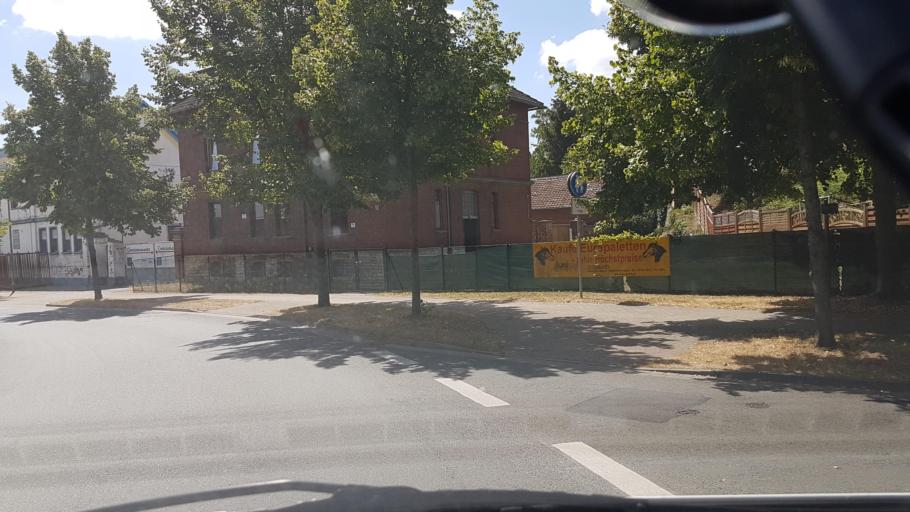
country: DE
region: Lower Saxony
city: Schoningen
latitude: 52.1327
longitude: 10.9734
